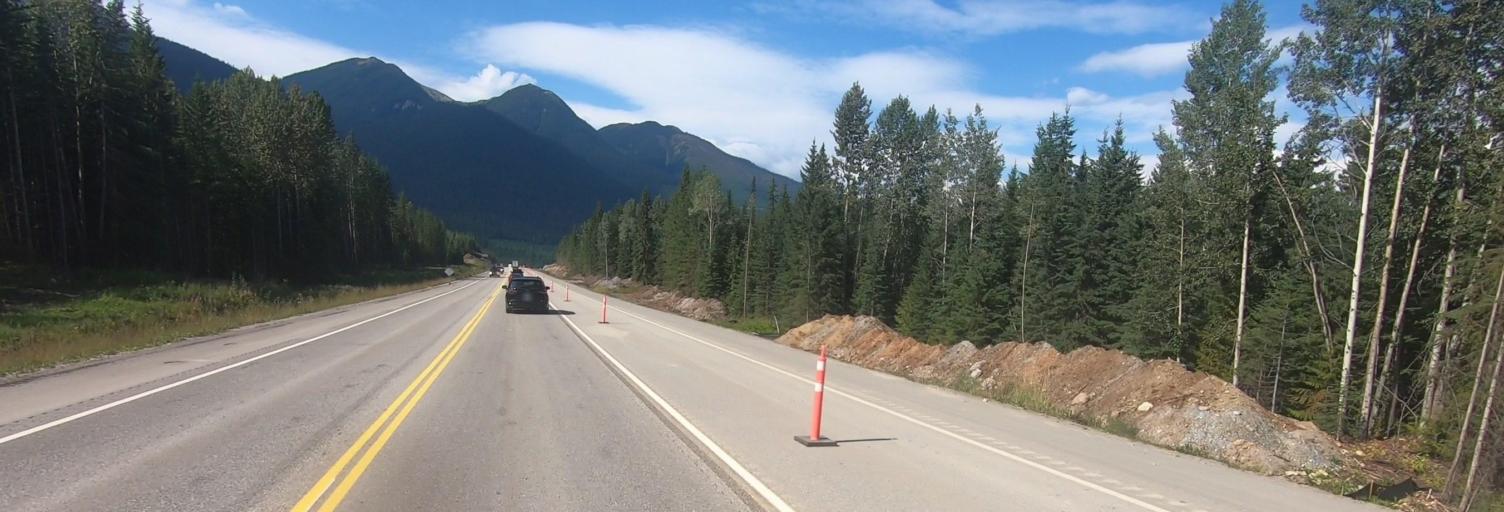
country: CA
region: British Columbia
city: Golden
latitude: 51.4826
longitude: -117.3407
